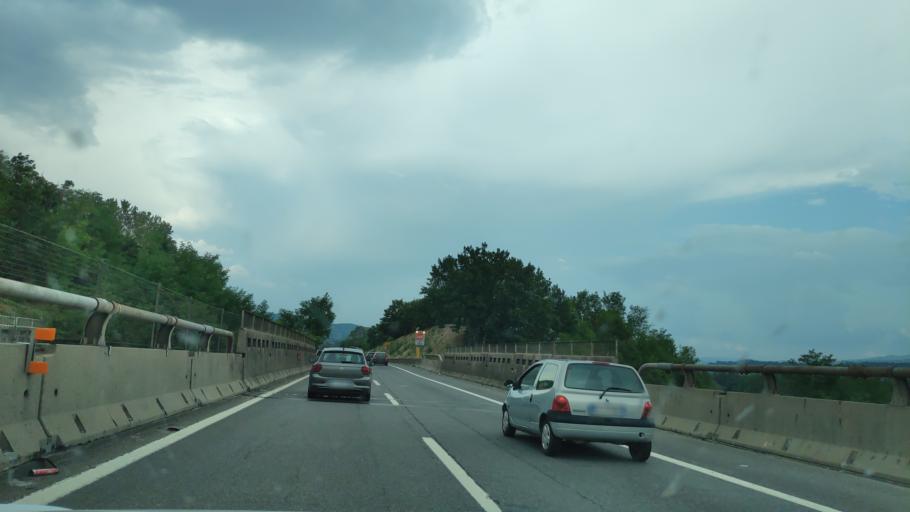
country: IT
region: Tuscany
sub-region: Province of Florence
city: Incisa in Val d'Arno
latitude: 43.6766
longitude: 11.4533
